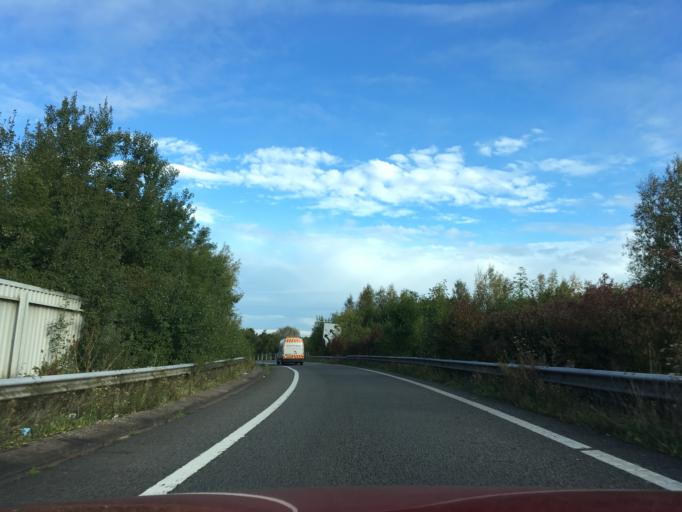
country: GB
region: England
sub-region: Gloucestershire
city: Churchdown
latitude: 51.8575
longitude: -2.1779
